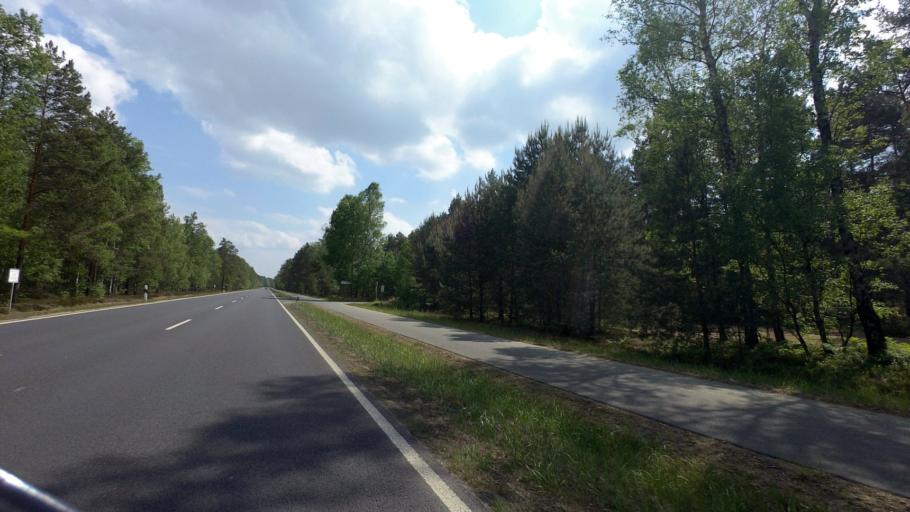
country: DE
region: Saxony
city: Rietschen
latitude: 51.4502
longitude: 14.7672
